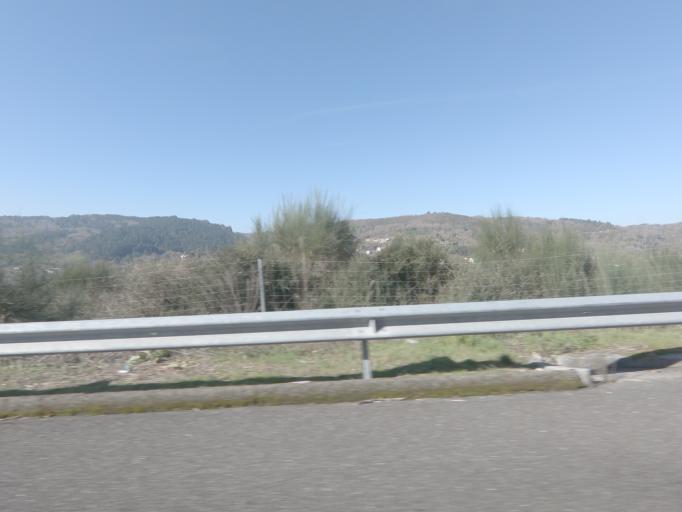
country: ES
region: Galicia
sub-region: Provincia de Ourense
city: Punxin
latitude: 42.3810
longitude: -7.9897
